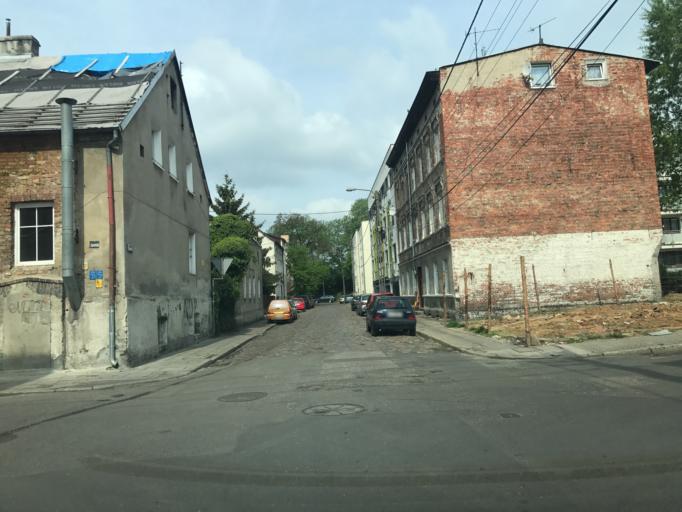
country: PL
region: Kujawsko-Pomorskie
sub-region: Bydgoszcz
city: Bydgoszcz
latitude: 53.1309
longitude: 17.9838
